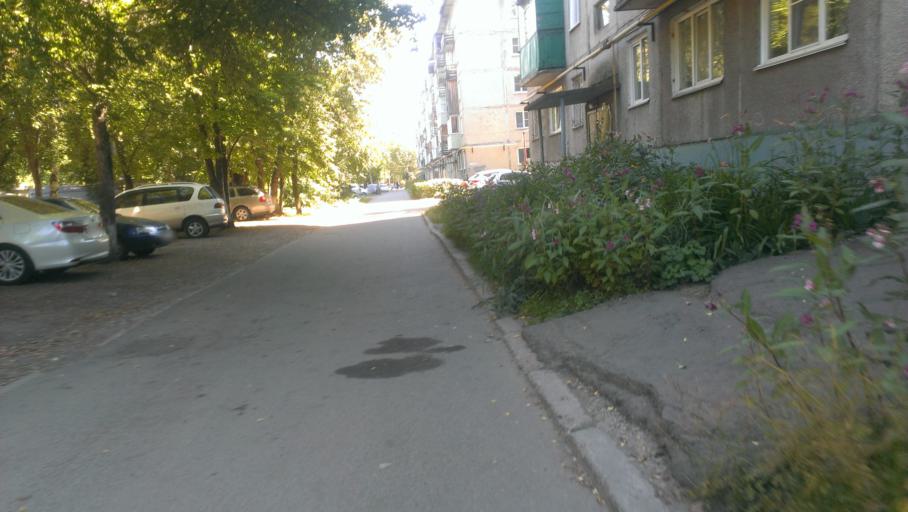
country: RU
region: Altai Krai
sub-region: Gorod Barnaulskiy
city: Barnaul
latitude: 53.3610
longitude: 83.6971
